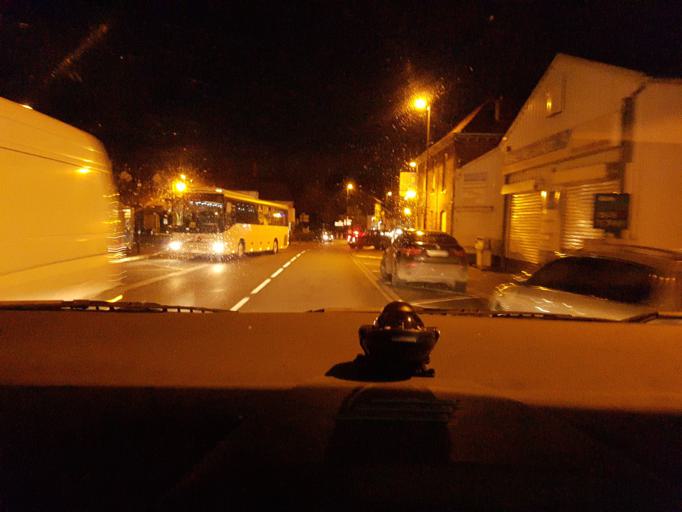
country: FR
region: Nord-Pas-de-Calais
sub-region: Departement du Pas-de-Calais
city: Souchez
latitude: 50.3908
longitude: 2.7420
